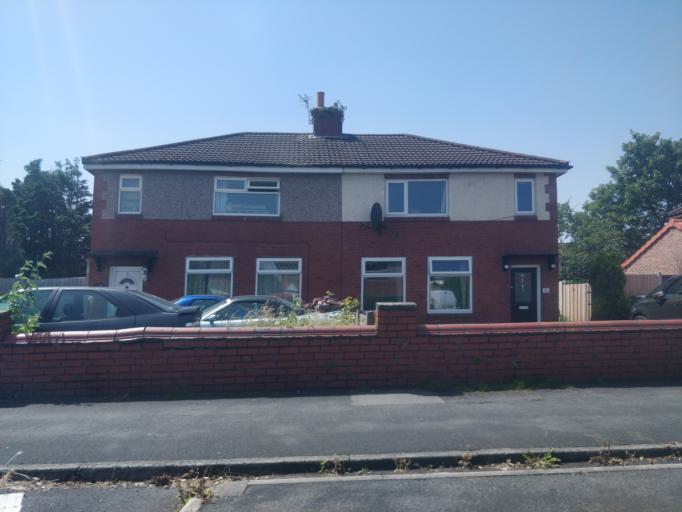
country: GB
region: England
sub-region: Sefton
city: Southport
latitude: 53.6449
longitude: -2.9682
